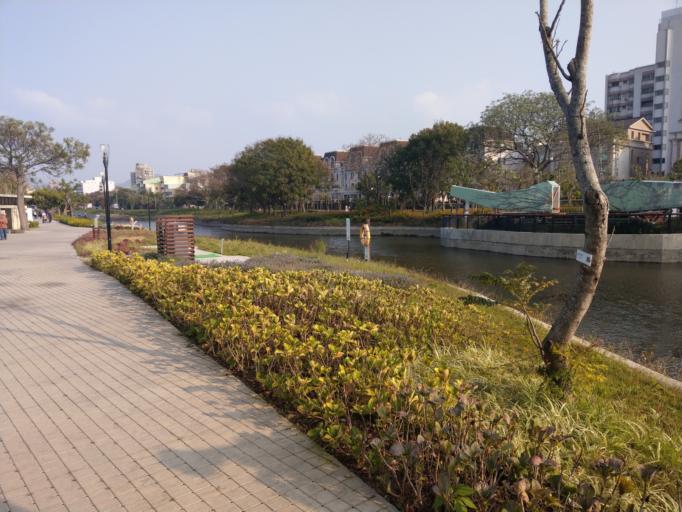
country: TW
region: Taiwan
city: Fengyuan
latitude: 24.2563
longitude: 120.7068
